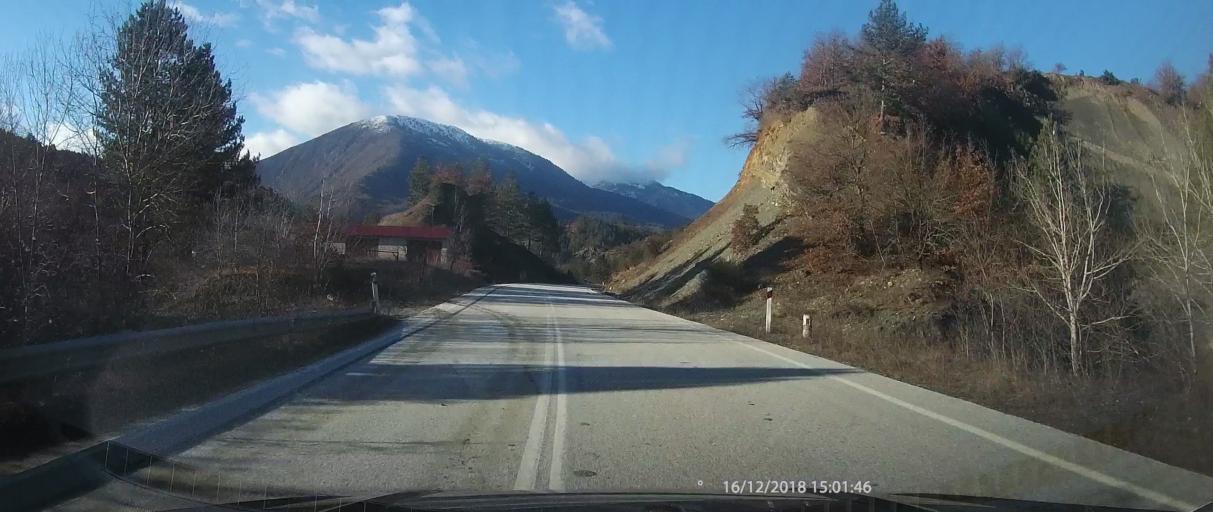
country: GR
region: West Macedonia
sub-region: Nomos Kastorias
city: Nestorio
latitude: 40.2243
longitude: 21.0029
